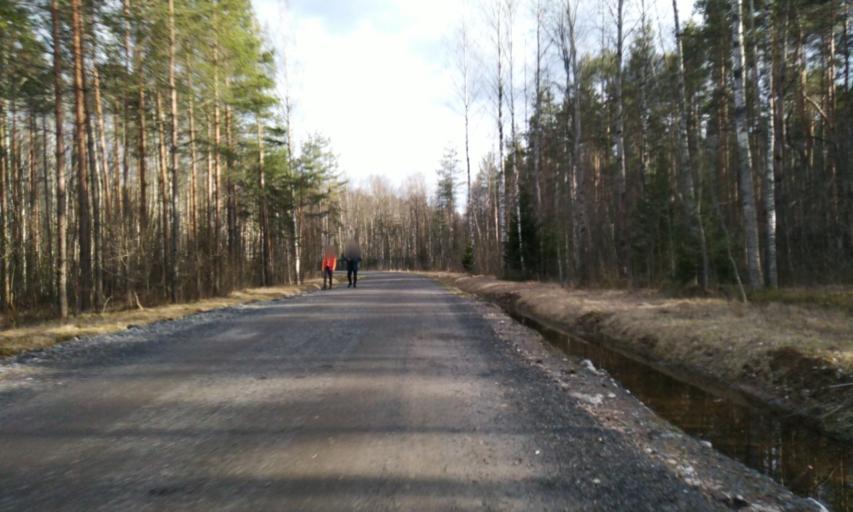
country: RU
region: Leningrad
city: Toksovo
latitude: 60.1225
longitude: 30.4751
